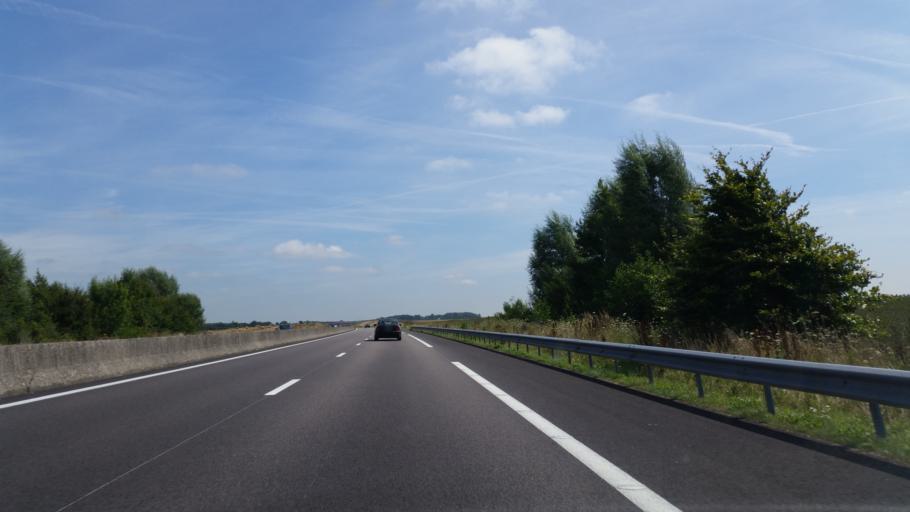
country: FR
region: Haute-Normandie
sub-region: Departement de la Seine-Maritime
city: Gaillefontaine
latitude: 49.7385
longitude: 1.6288
